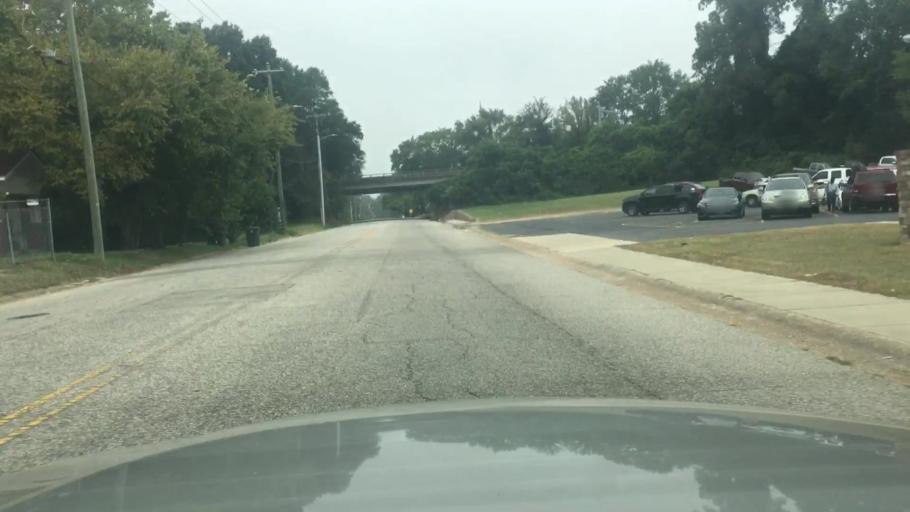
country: US
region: North Carolina
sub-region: Cumberland County
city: Fayetteville
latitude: 35.0663
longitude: -78.8849
